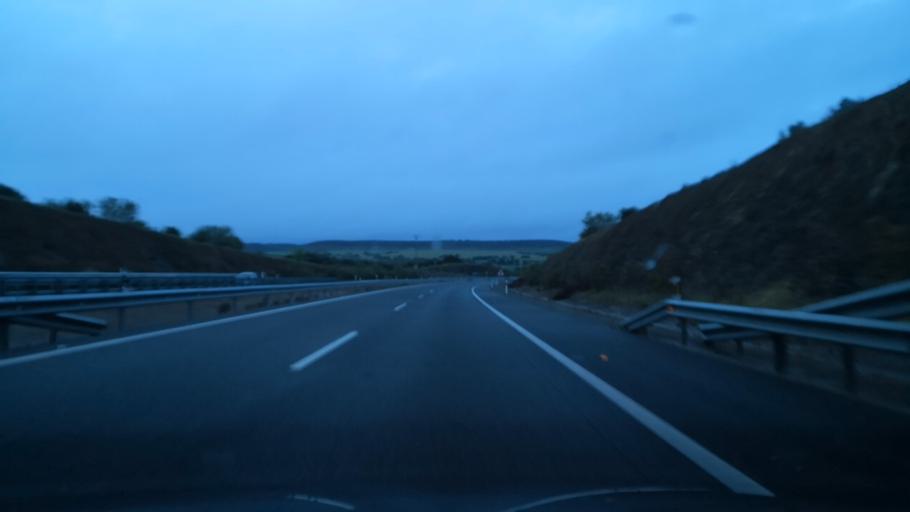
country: ES
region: Extremadura
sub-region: Provincia de Badajoz
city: Aljucen
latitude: 39.0389
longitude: -6.3381
